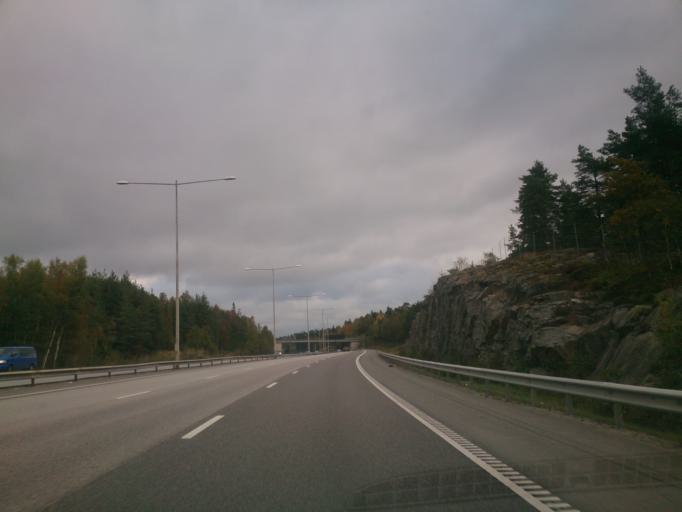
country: SE
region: Stockholm
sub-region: Haninge Kommun
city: Handen
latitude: 59.2122
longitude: 18.1318
